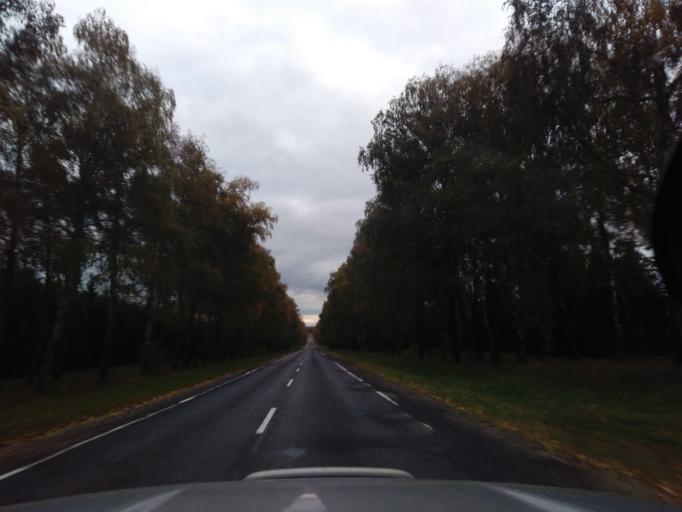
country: BY
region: Minsk
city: Slutsk
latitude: 53.2203
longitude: 27.4703
